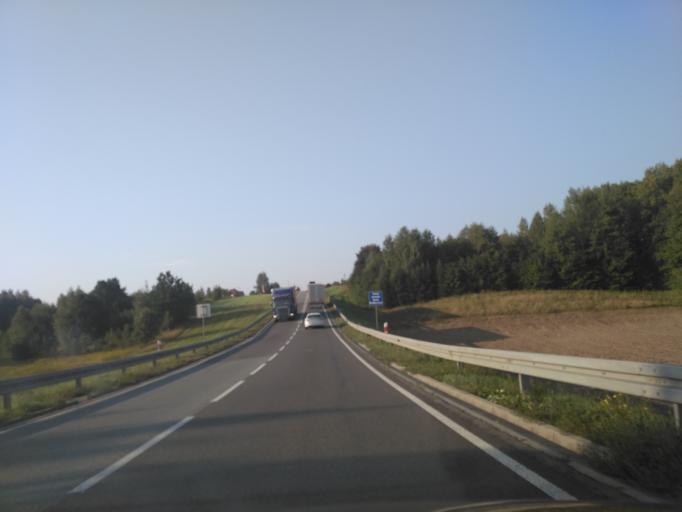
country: PL
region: Lublin Voivodeship
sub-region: Powiat janowski
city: Modliborzyce
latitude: 50.7994
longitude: 22.3188
